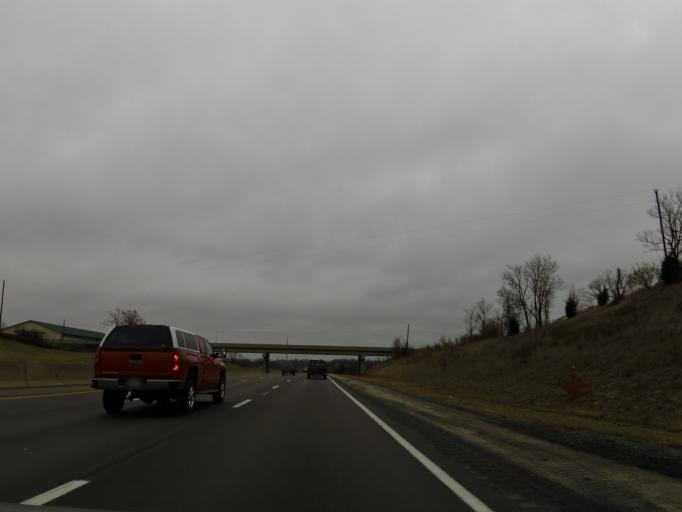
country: US
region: Kentucky
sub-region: Grant County
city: Dry Ridge
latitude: 38.7109
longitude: -84.6033
